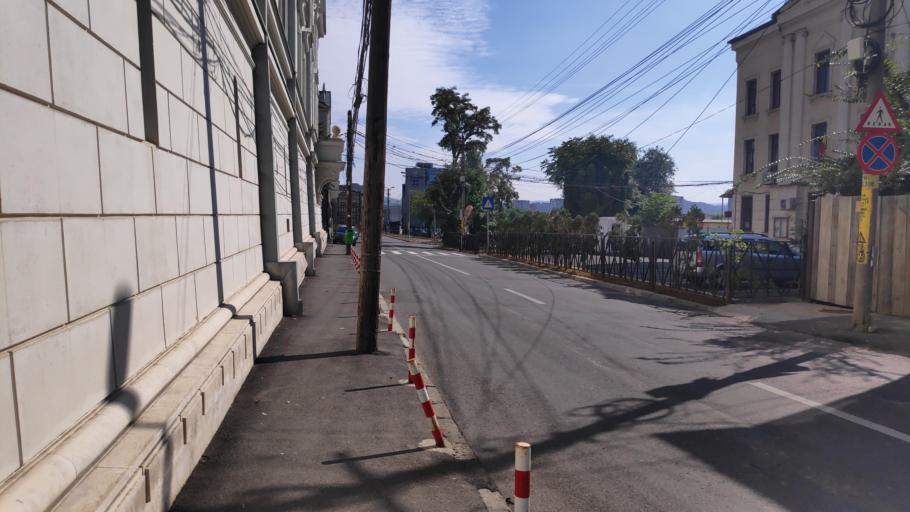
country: RO
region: Iasi
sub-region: Municipiul Iasi
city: Iasi
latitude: 47.1616
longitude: 27.5806
